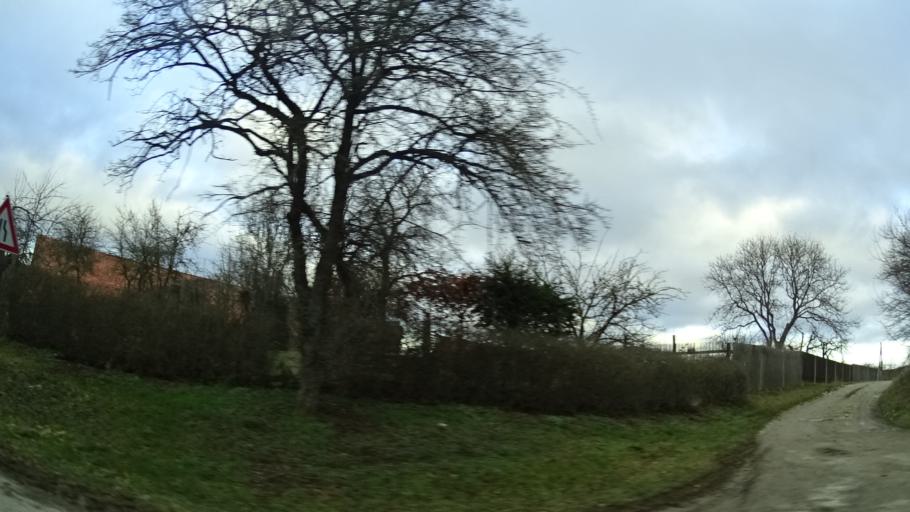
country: DE
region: Thuringia
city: Rittersdorf
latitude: 50.7459
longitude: 11.2129
